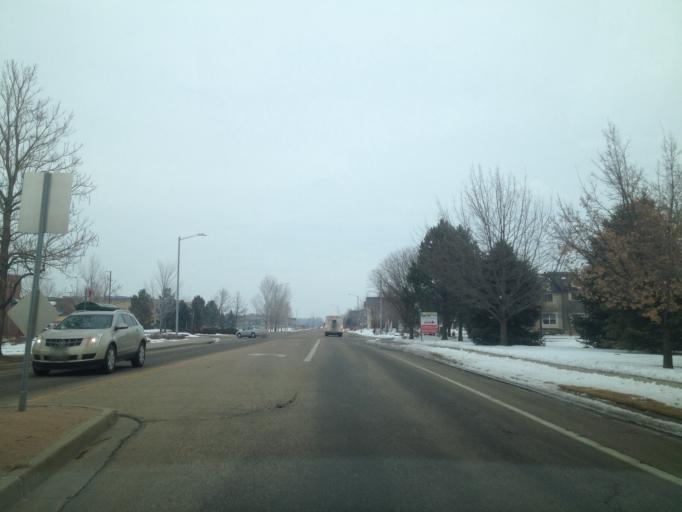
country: US
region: Colorado
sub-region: Boulder County
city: Longmont
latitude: 40.1451
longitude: -105.1000
